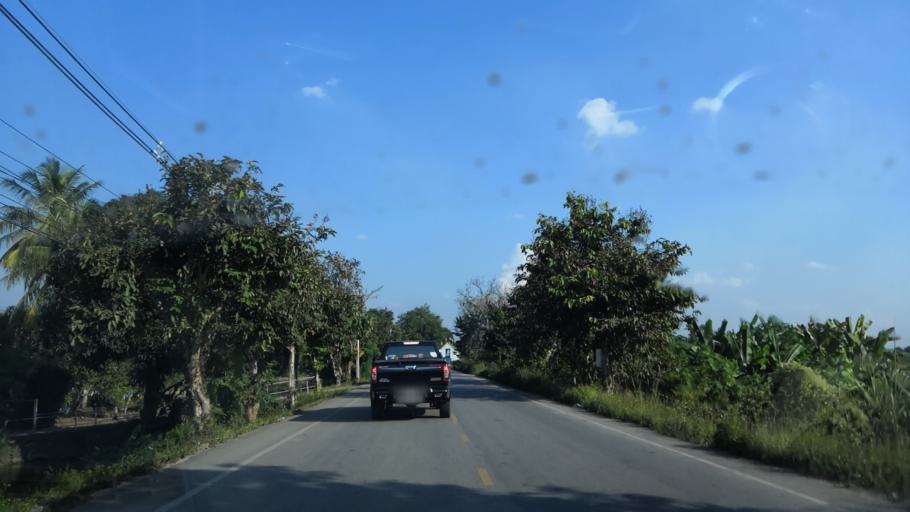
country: TH
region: Chiang Rai
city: Wiang Chai
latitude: 19.9328
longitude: 99.8922
